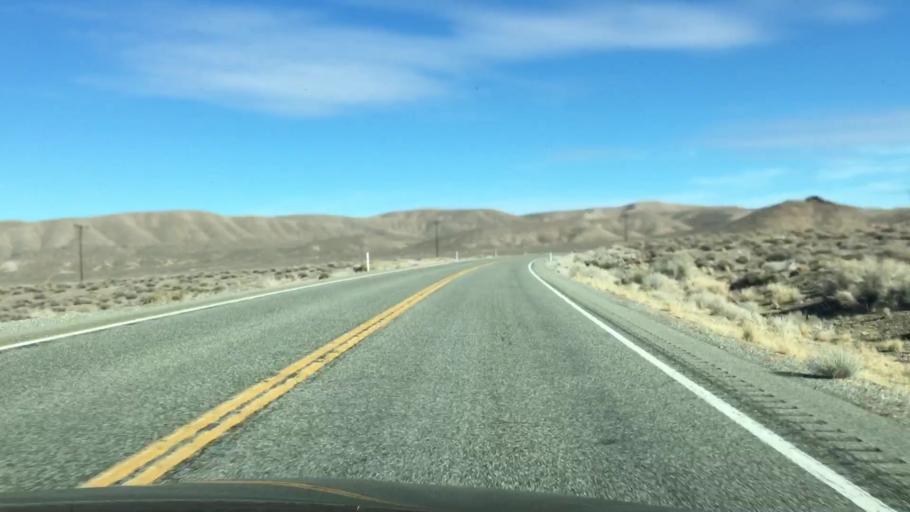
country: US
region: Nevada
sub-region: Lyon County
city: Yerington
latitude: 39.0456
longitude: -118.9763
